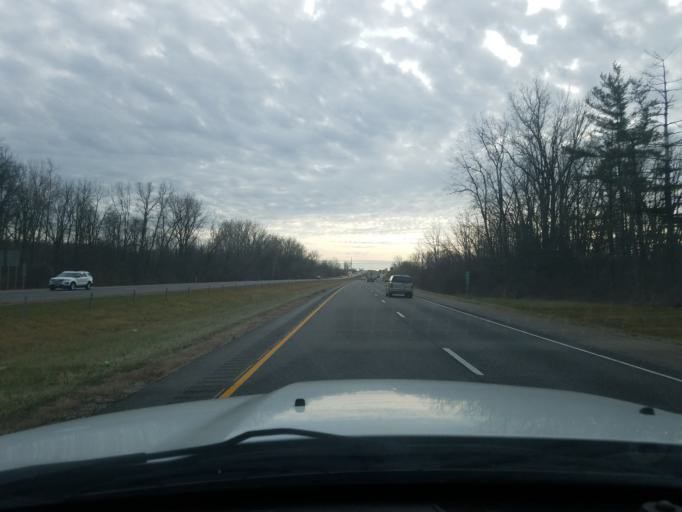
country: US
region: Indiana
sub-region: Delaware County
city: Yorktown
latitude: 40.2347
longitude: -85.5576
